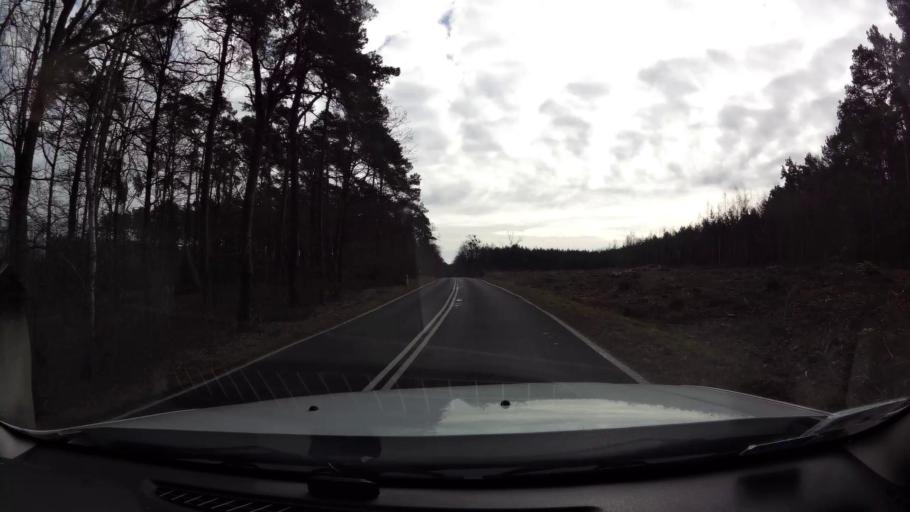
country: PL
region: West Pomeranian Voivodeship
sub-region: Powiat mysliborski
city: Debno
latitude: 52.7703
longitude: 14.6664
